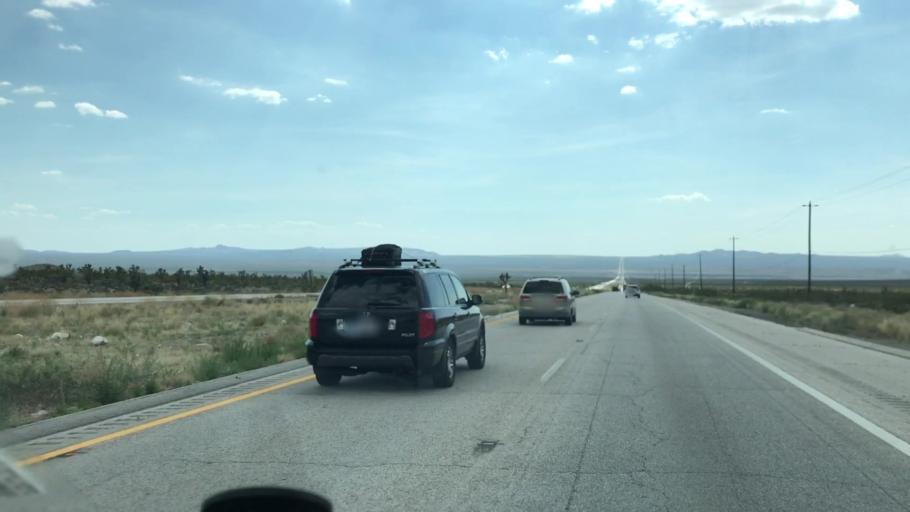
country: US
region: Nevada
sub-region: Clark County
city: Sandy Valley
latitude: 35.4726
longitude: -115.5938
